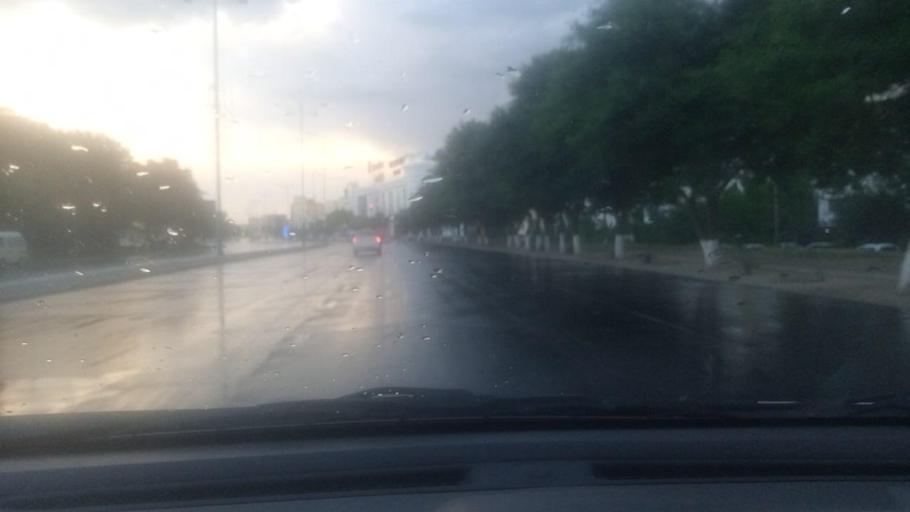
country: UZ
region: Toshkent Shahri
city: Tashkent
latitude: 41.3128
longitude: 69.2384
